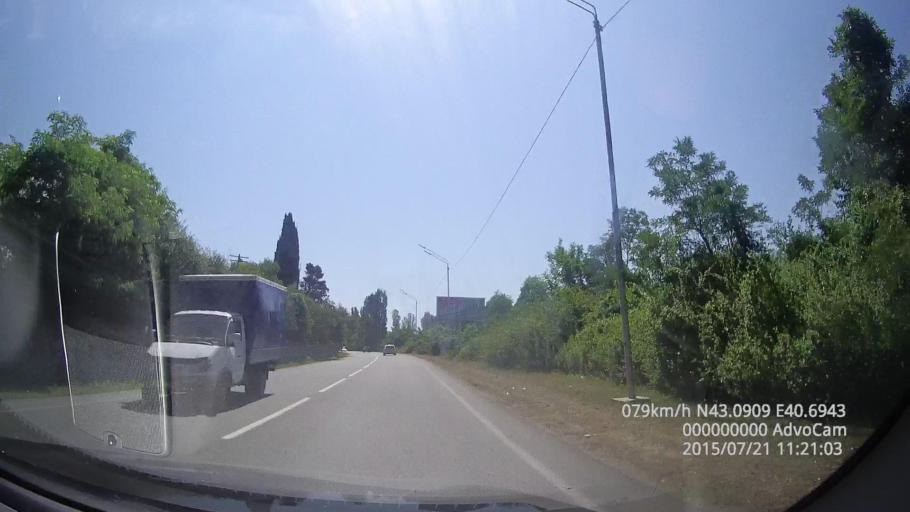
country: GE
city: P'rimorsk'oe
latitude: 43.0906
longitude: 40.6947
